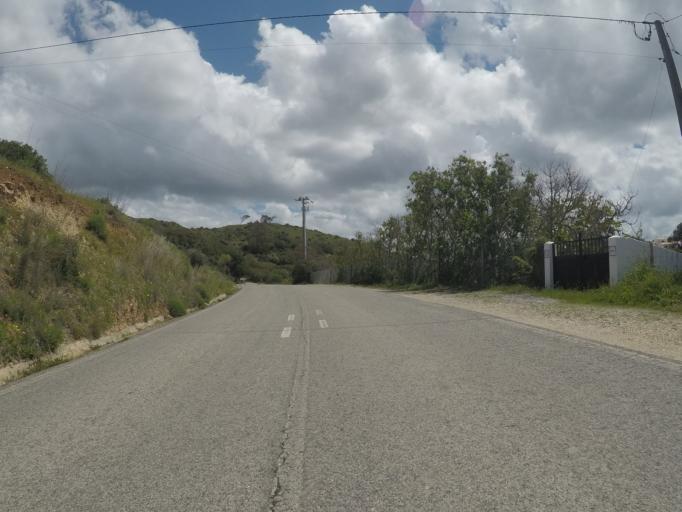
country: PT
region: Faro
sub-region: Vila do Bispo
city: Vila do Bispo
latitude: 37.0775
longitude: -8.8335
